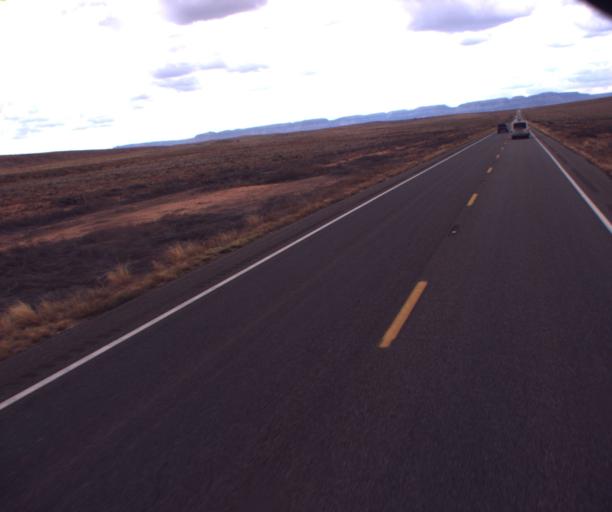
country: US
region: Arizona
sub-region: Navajo County
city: Kayenta
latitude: 36.7546
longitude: -110.0549
